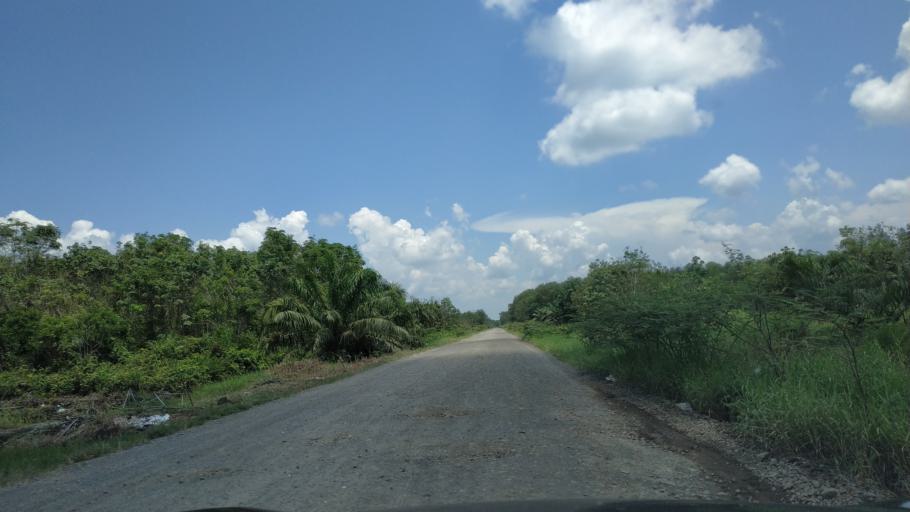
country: ID
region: Riau
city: Pangkalanbunut
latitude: 0.1972
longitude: 102.3901
